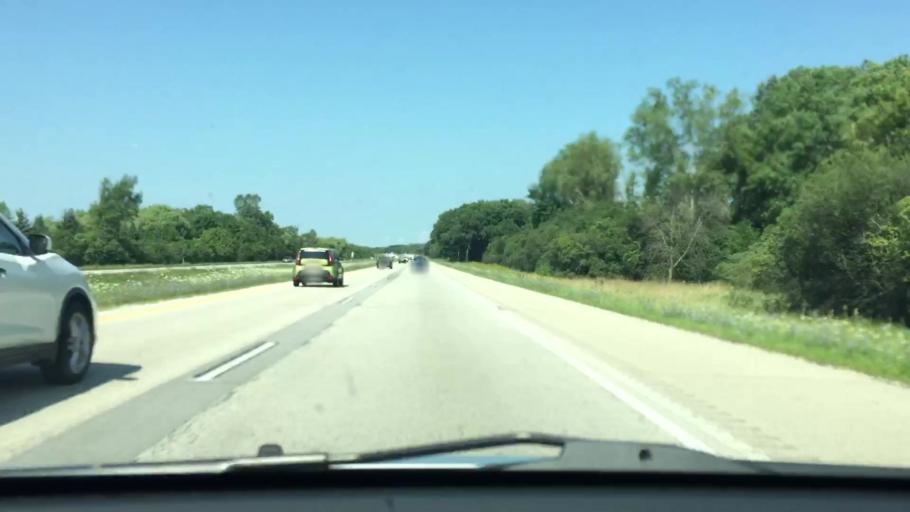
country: US
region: Wisconsin
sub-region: Waukesha County
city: Oconomowoc
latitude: 43.0696
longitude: -88.5035
